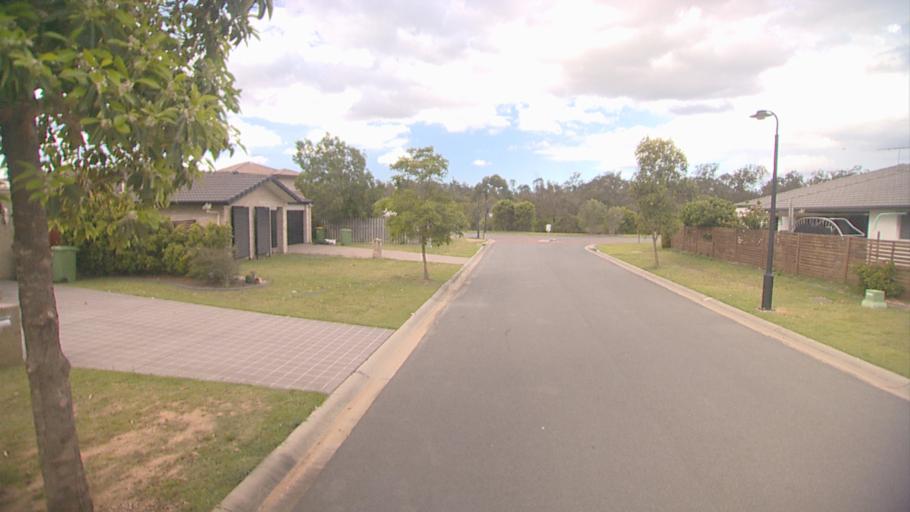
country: AU
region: Queensland
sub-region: Logan
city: Woodridge
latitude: -27.6598
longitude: 153.0764
